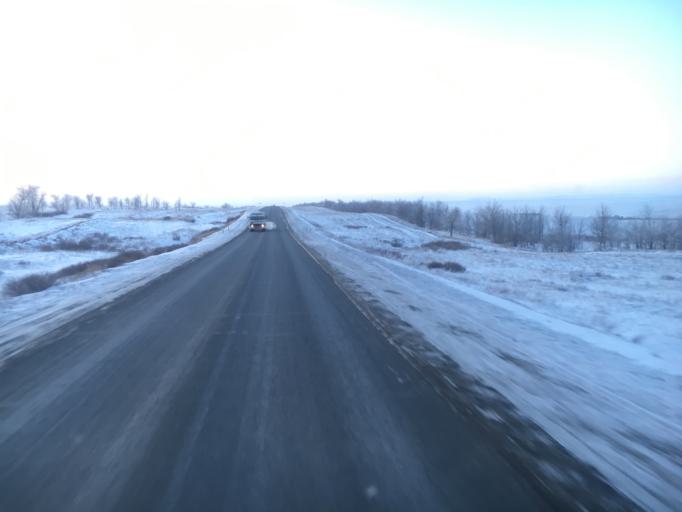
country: KZ
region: Aqtoebe
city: Aqtobe
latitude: 50.2841
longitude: 57.7348
